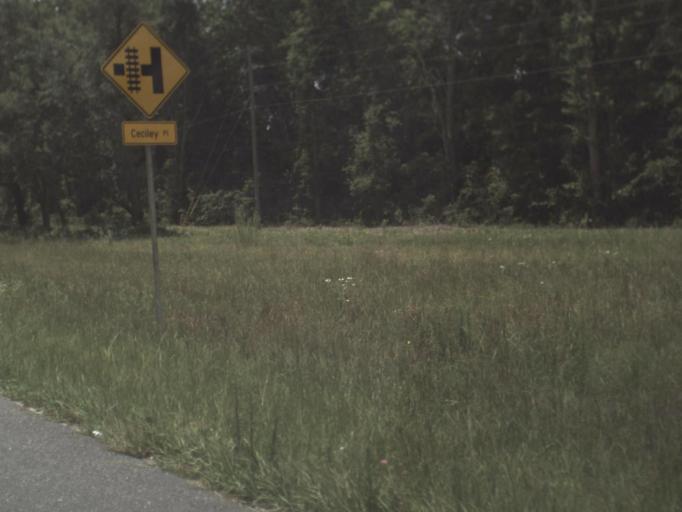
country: US
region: Florida
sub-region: Columbia County
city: Five Points
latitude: 30.3112
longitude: -82.7133
